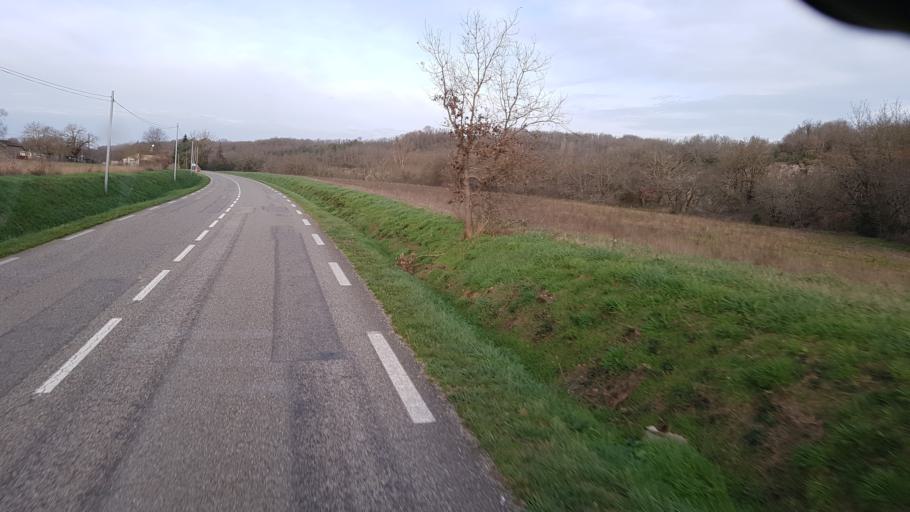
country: FR
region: Midi-Pyrenees
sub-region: Departement du Tarn-et-Garonne
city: Montricoux
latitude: 44.0724
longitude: 1.6444
